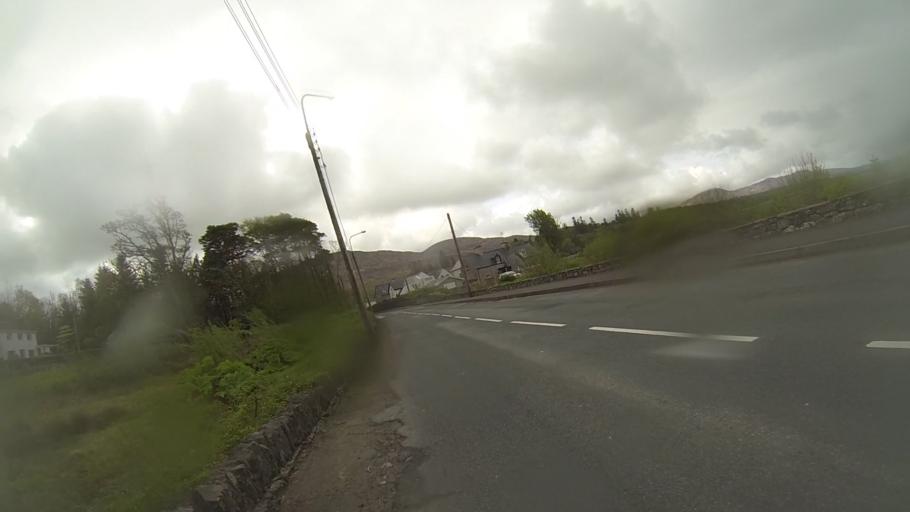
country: IE
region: Munster
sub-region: Ciarrai
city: Kenmare
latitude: 51.8740
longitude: -9.5837
